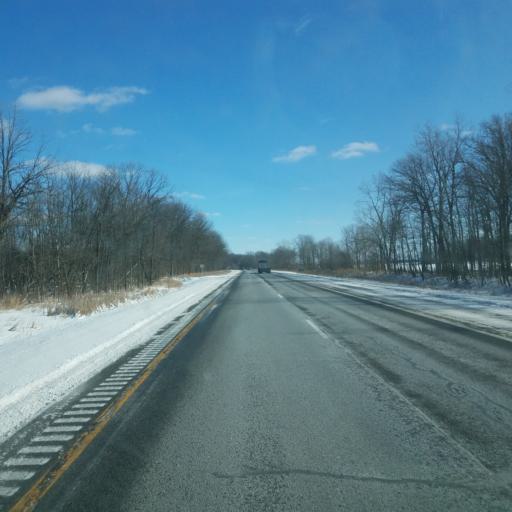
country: US
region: Michigan
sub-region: Ingham County
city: Williamston
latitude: 42.6662
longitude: -84.3376
